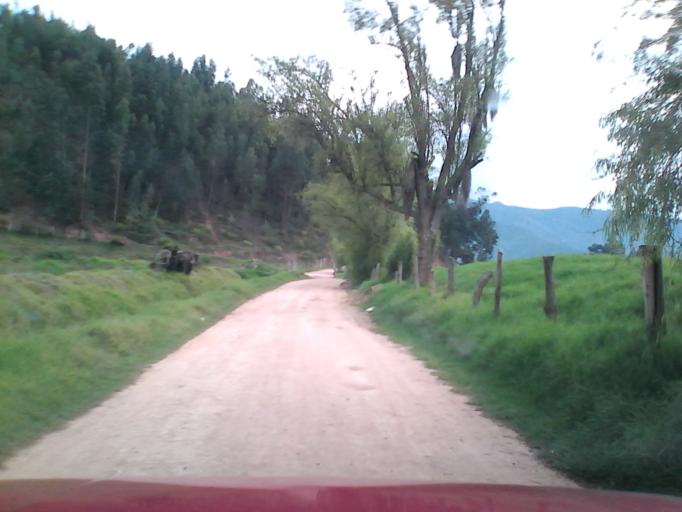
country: CO
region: Boyaca
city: Duitama
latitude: 5.8084
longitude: -72.9979
